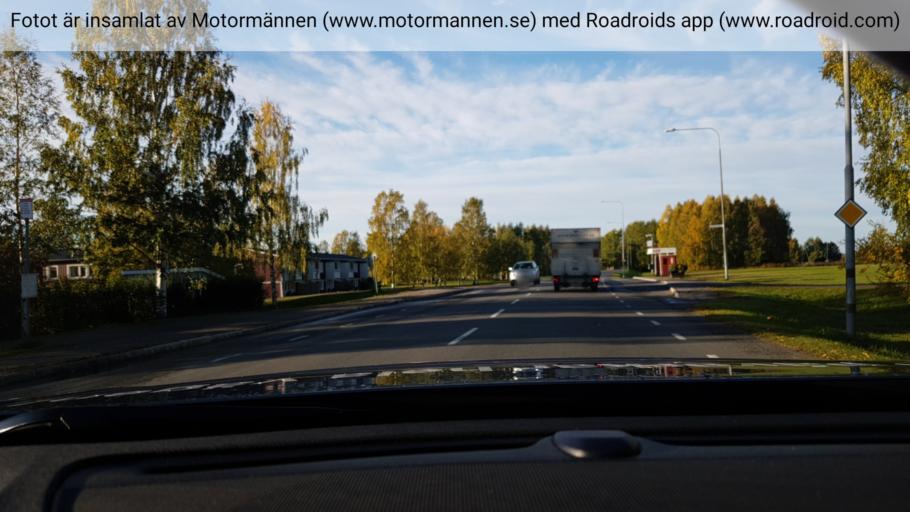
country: SE
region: Norrbotten
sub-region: Lulea Kommun
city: Sodra Sunderbyn
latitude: 65.6580
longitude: 21.9507
